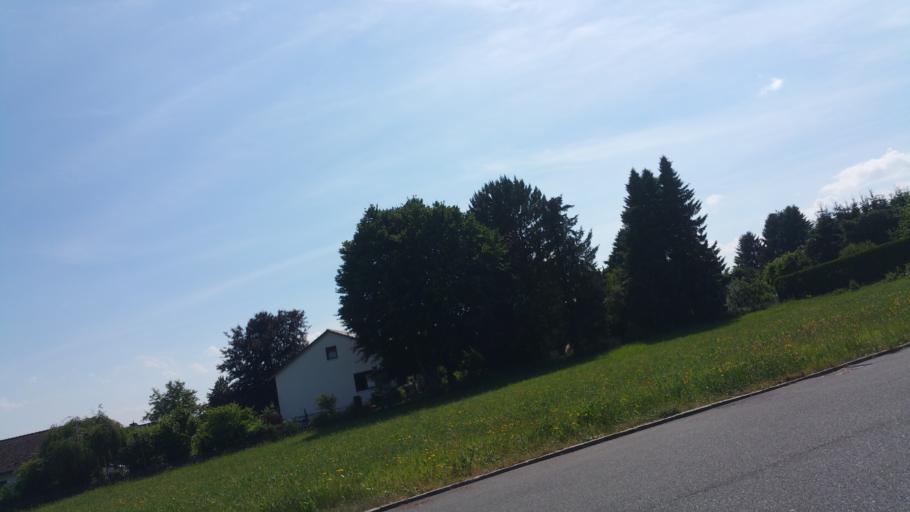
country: DE
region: Bavaria
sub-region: Upper Franconia
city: Schwarzenbach an der Saale
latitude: 50.2126
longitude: 11.9124
